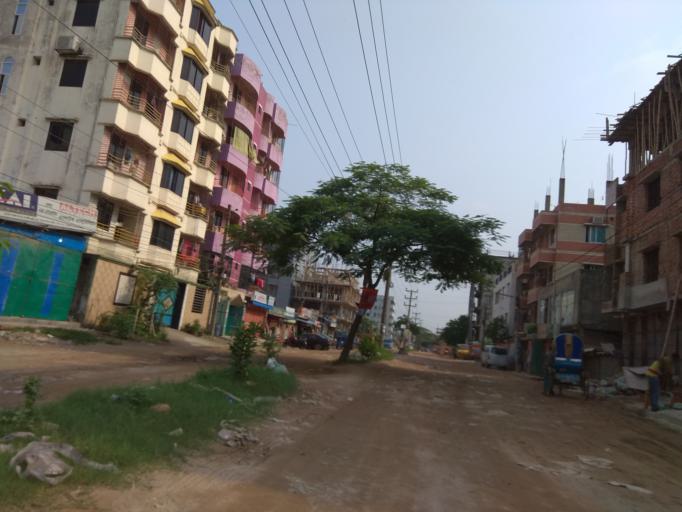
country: BD
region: Dhaka
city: Tungi
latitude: 23.8256
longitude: 90.3534
